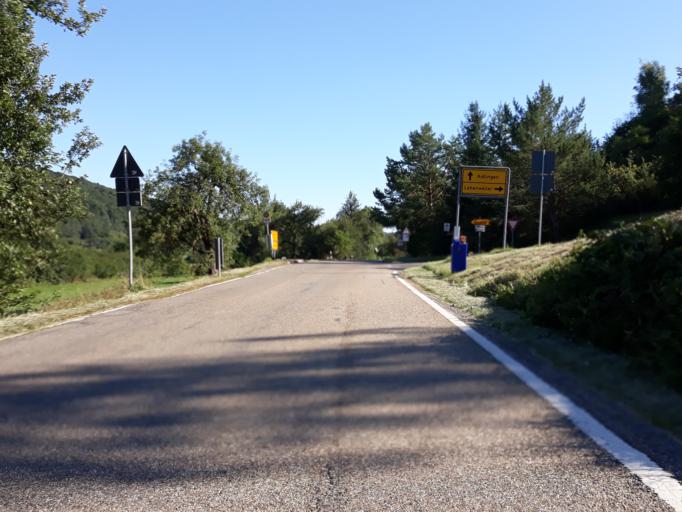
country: DE
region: Baden-Wuerttemberg
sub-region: Regierungsbezirk Stuttgart
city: Aidlingen
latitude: 48.6969
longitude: 8.8957
